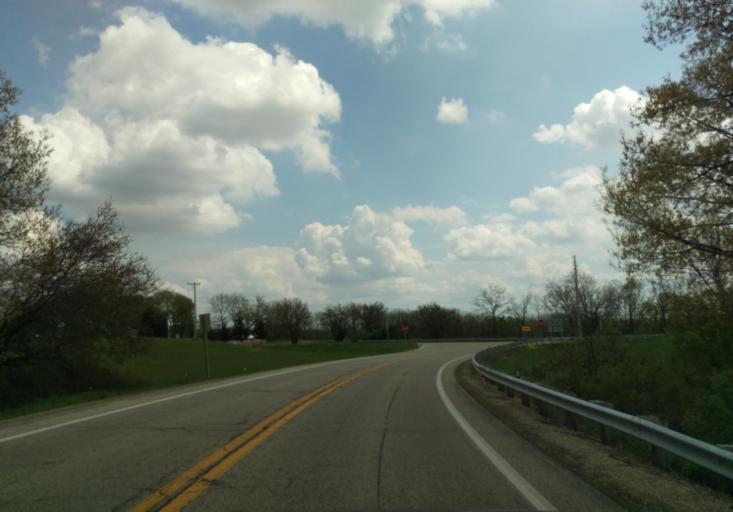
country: US
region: Wisconsin
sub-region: Green County
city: New Glarus
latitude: 42.8669
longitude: -89.6028
